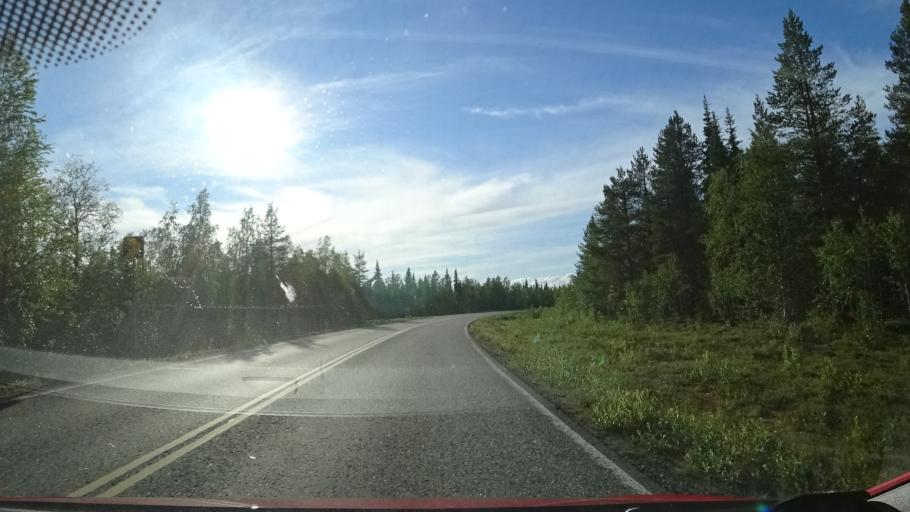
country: FI
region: Lapland
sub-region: Pohjois-Lappi
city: Sodankylae
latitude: 67.8351
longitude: 26.7237
